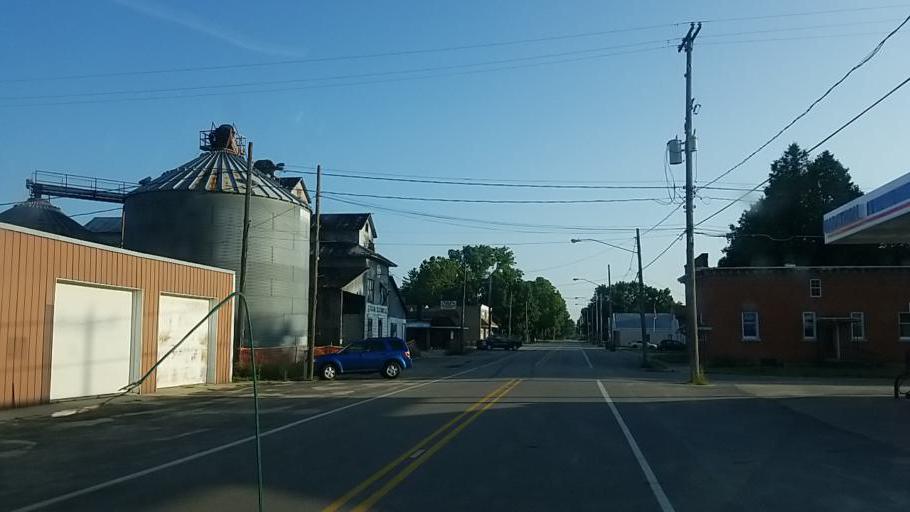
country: US
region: Michigan
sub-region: Montcalm County
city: Howard City
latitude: 43.3618
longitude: -85.4029
